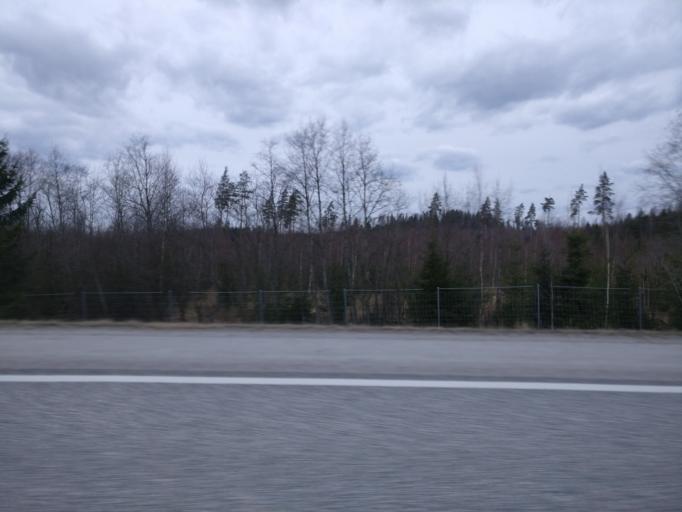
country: FI
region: Uusimaa
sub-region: Helsinki
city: Hyvinge
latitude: 60.6093
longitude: 24.8035
